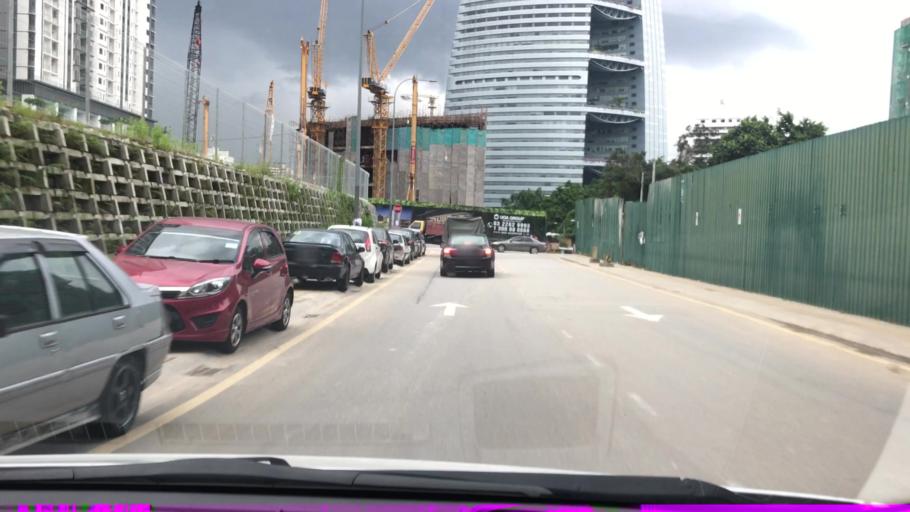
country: MY
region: Kuala Lumpur
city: Kuala Lumpur
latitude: 3.1123
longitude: 101.6655
